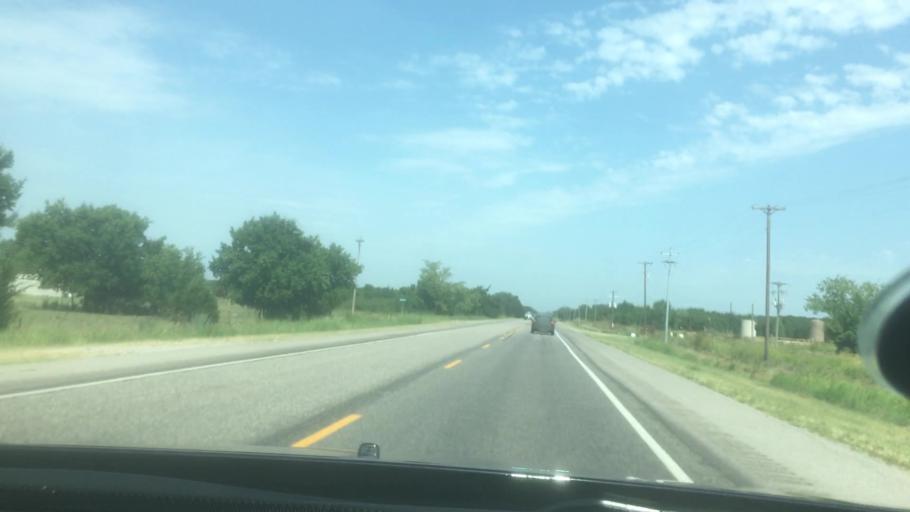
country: US
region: Oklahoma
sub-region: Seminole County
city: Konawa
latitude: 34.8702
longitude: -96.8414
